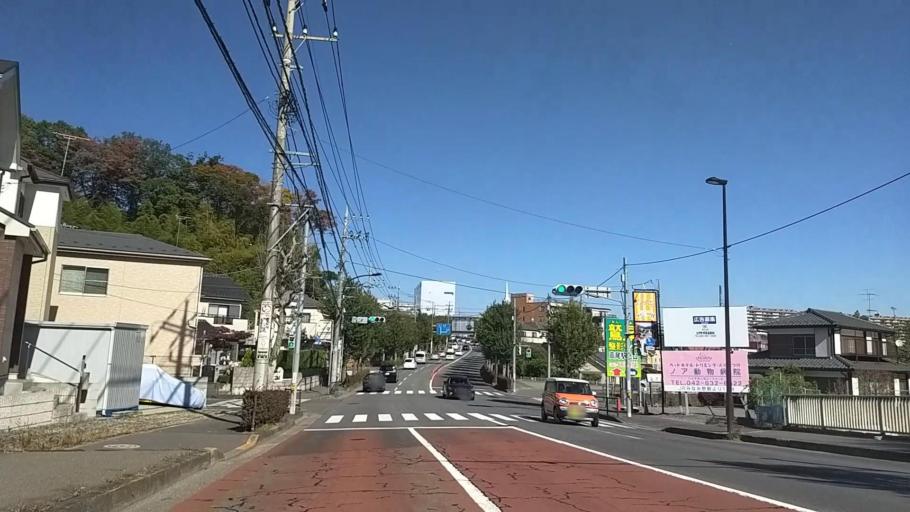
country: JP
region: Tokyo
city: Hachioji
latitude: 35.6329
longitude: 139.2868
